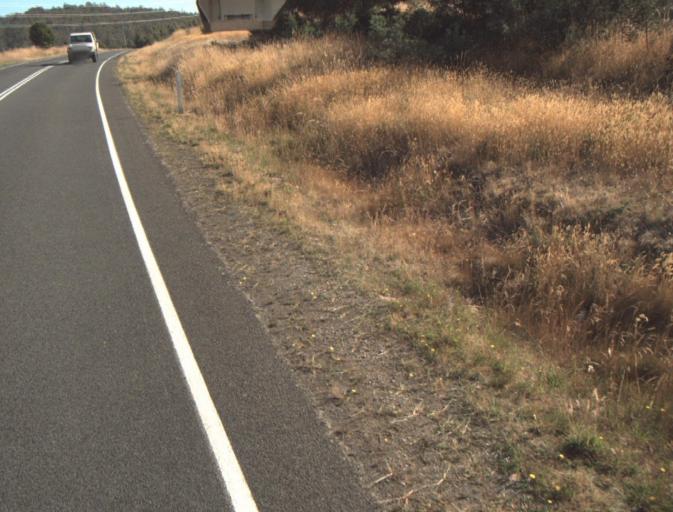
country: AU
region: Tasmania
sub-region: Launceston
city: Newstead
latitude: -41.4126
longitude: 147.2804
